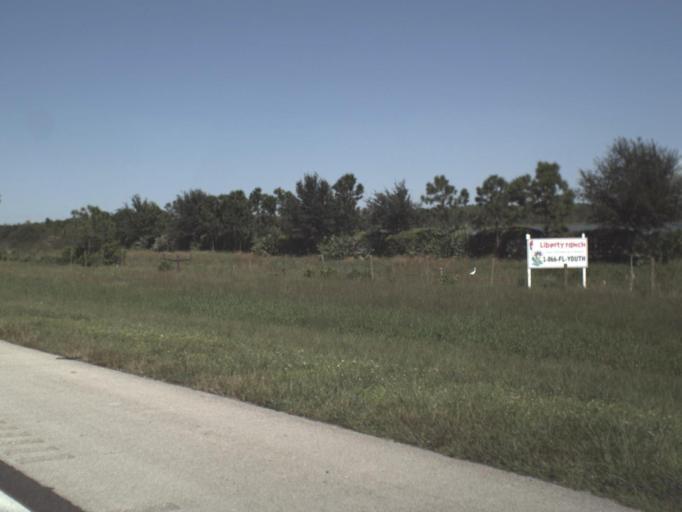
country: US
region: Florida
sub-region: Lee County
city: Bonita Springs
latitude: 26.3756
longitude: -81.7715
